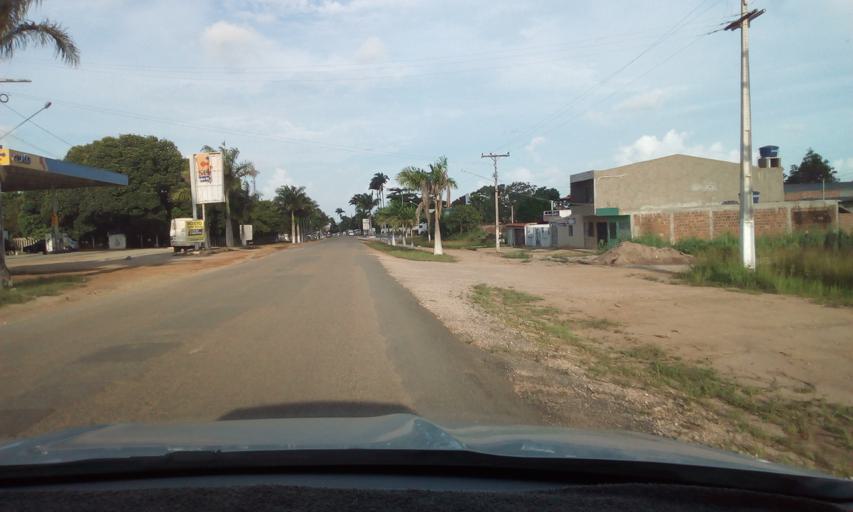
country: BR
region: Pernambuco
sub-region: Gloria Do Goita
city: Gloria do Goita
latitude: -7.9980
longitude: -35.2194
